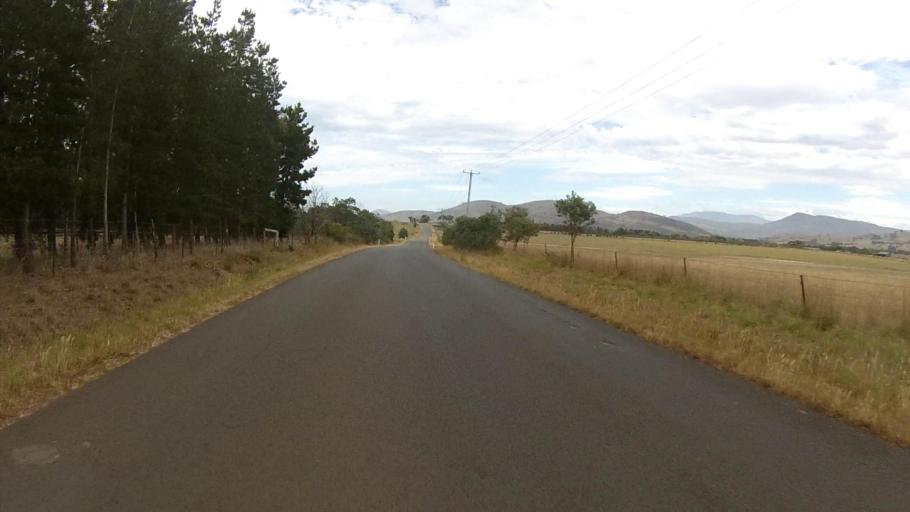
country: AU
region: Tasmania
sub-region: Clarence
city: Cambridge
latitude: -42.7184
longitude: 147.4517
